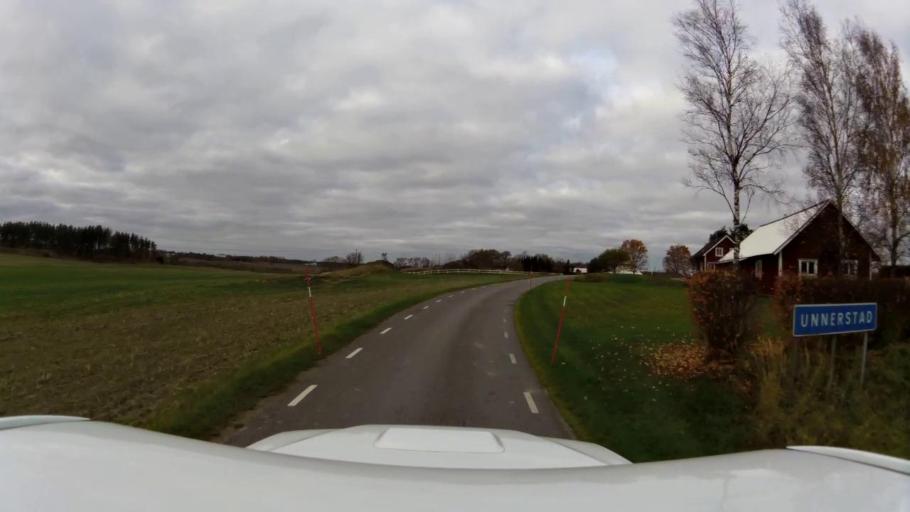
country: SE
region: OEstergoetland
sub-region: Linkopings Kommun
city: Linghem
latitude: 58.3969
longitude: 15.7899
